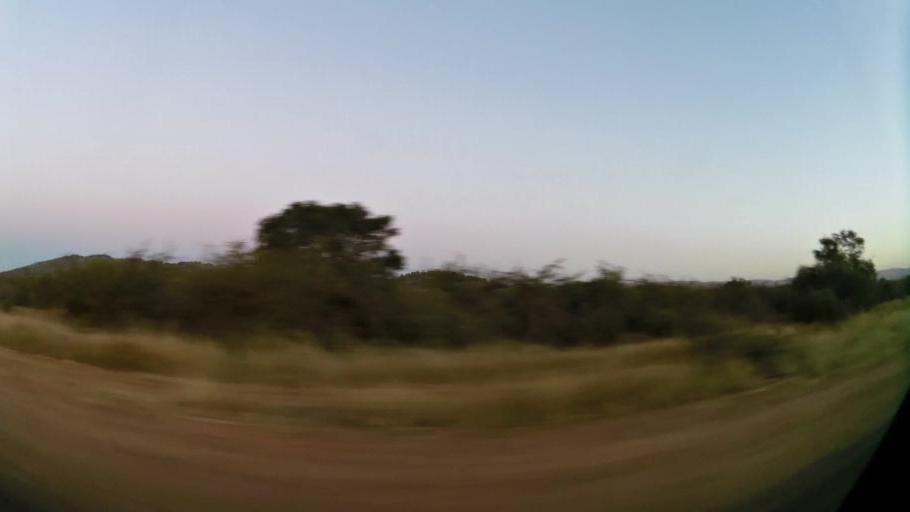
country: ZA
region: North-West
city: Ga-Rankuwa
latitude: -25.6302
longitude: 27.9599
